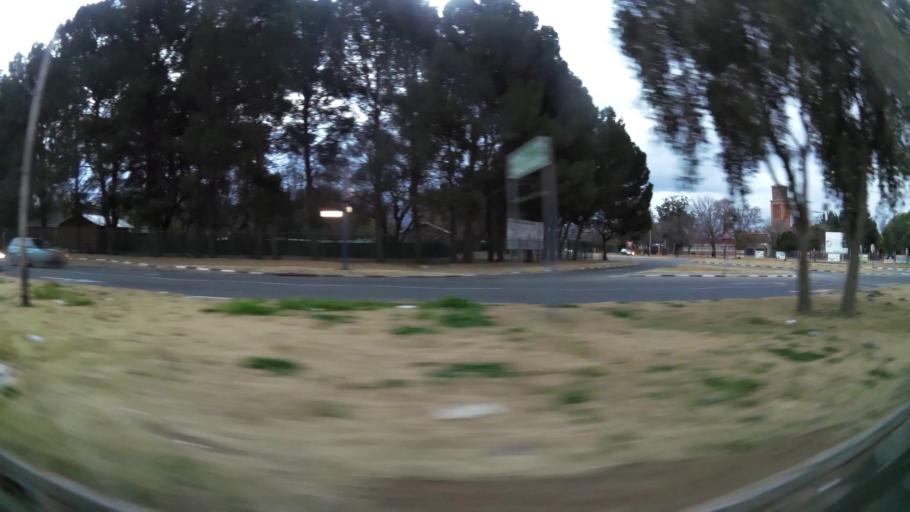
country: ZA
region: Orange Free State
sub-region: Lejweleputswa District Municipality
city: Welkom
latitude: -27.9748
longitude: 26.7457
